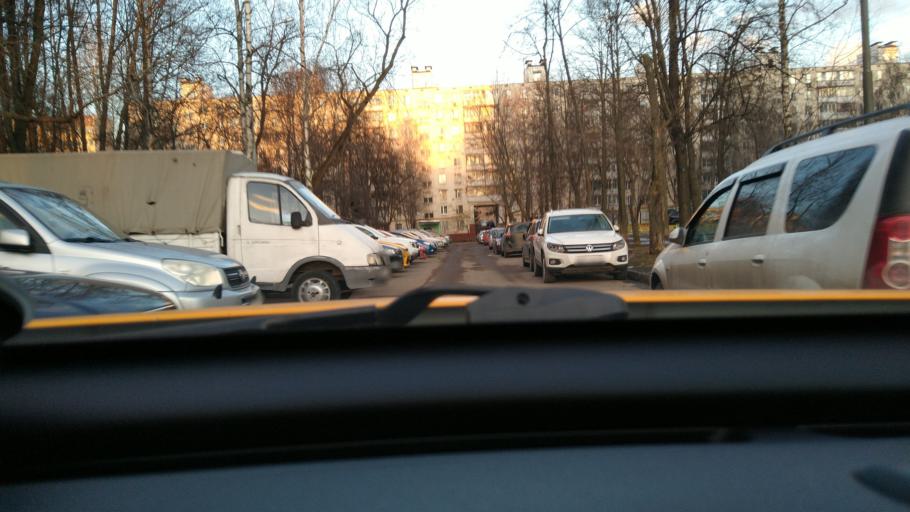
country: RU
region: Moscow
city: Strogino
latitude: 55.8527
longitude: 37.4349
